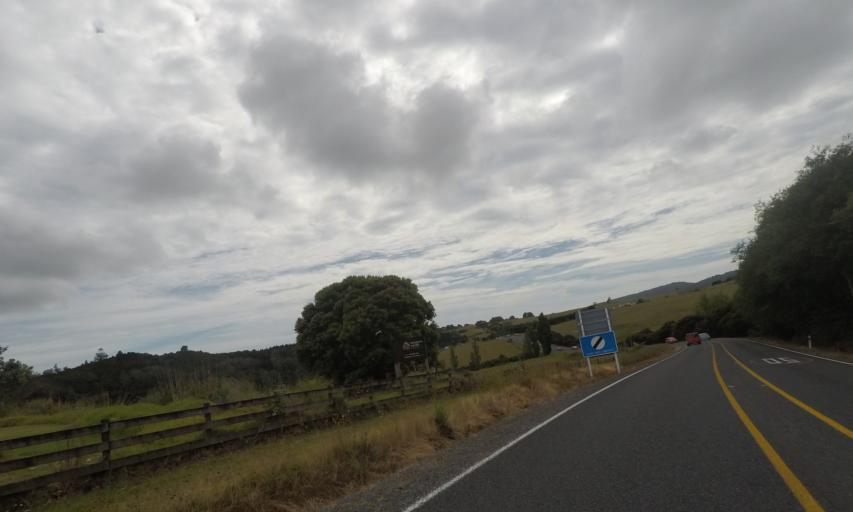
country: NZ
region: Northland
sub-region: Whangarei
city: Ruakaka
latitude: -35.7690
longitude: 174.4836
